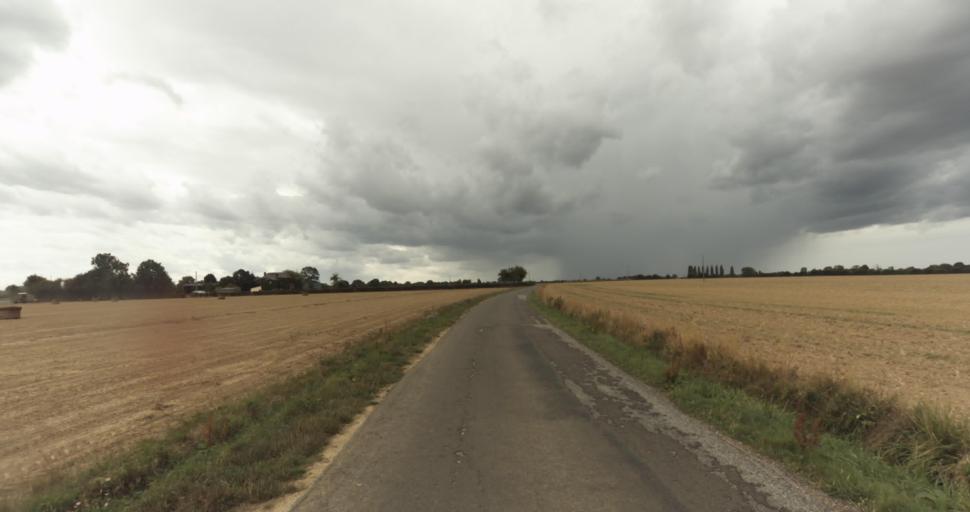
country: FR
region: Lower Normandy
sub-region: Departement du Calvados
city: Orbec
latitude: 48.9189
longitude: 0.3751
